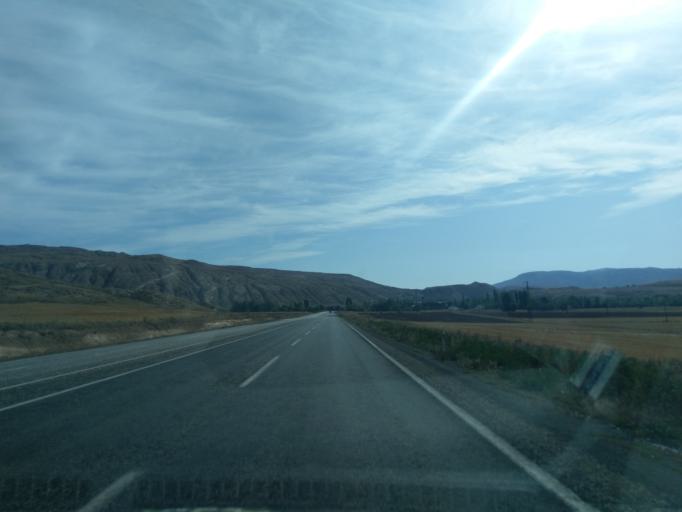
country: TR
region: Sivas
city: Zara
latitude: 39.8619
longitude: 37.8125
